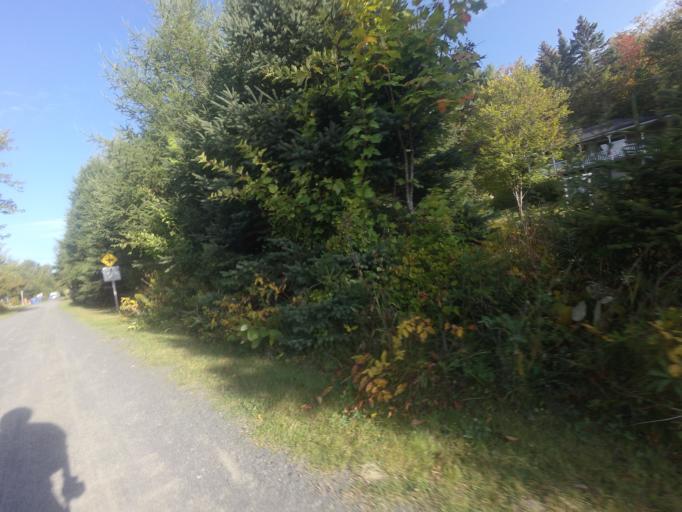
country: CA
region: Quebec
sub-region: Laurentides
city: Val-David
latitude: 46.0103
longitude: -74.1720
